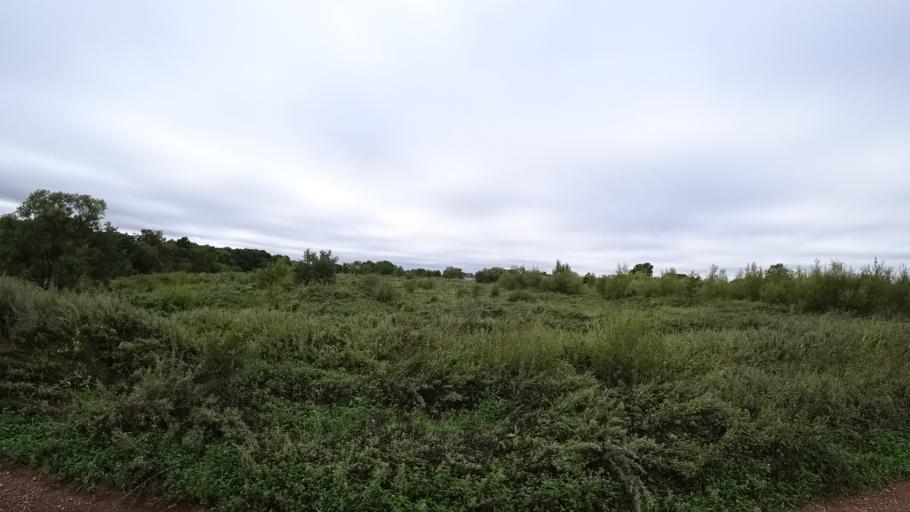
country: RU
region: Primorskiy
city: Monastyrishche
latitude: 44.1864
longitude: 132.4828
